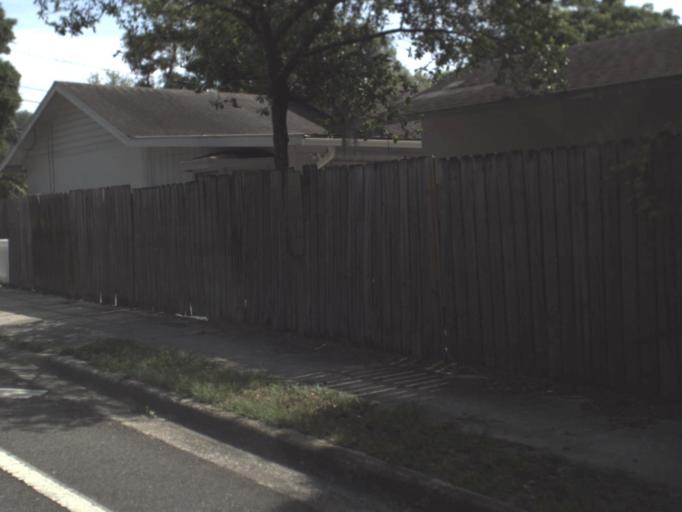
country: US
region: Florida
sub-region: Duval County
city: Jacksonville
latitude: 30.3195
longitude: -81.5986
